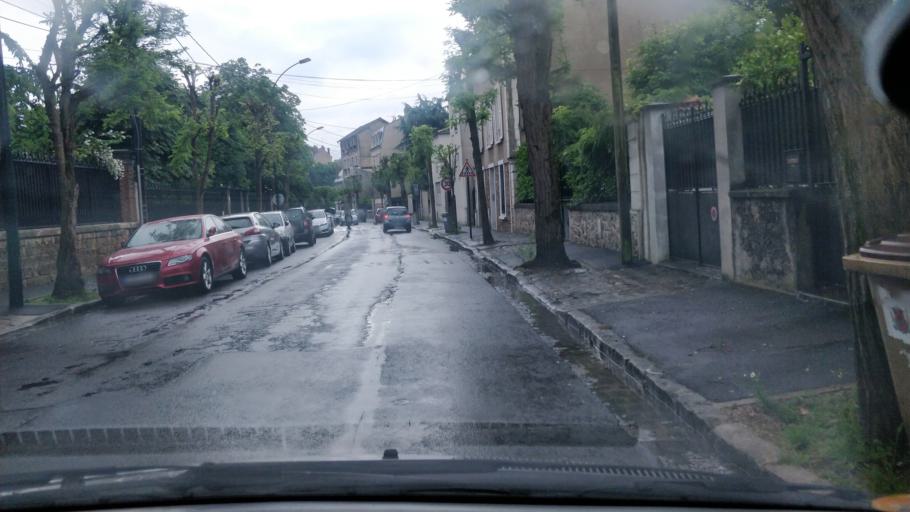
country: FR
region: Ile-de-France
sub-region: Departement de Seine-Saint-Denis
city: Le Raincy
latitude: 48.8946
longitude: 2.5090
